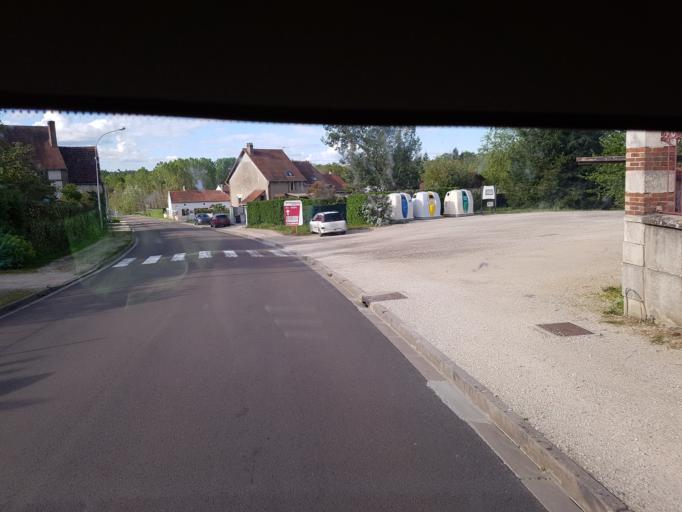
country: FR
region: Bourgogne
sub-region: Departement de l'Yonne
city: Vergigny
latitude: 47.9411
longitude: 3.7326
